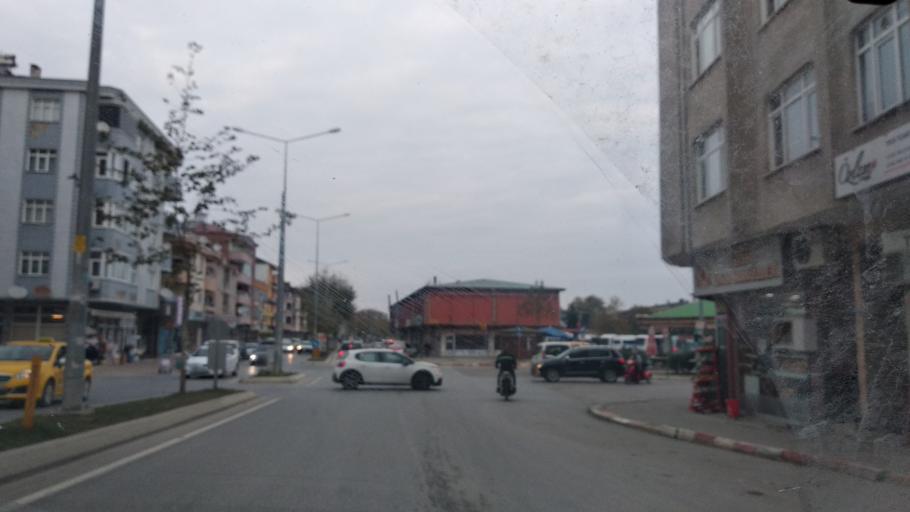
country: TR
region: Sakarya
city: Karasu
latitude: 41.0950
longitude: 30.6870
